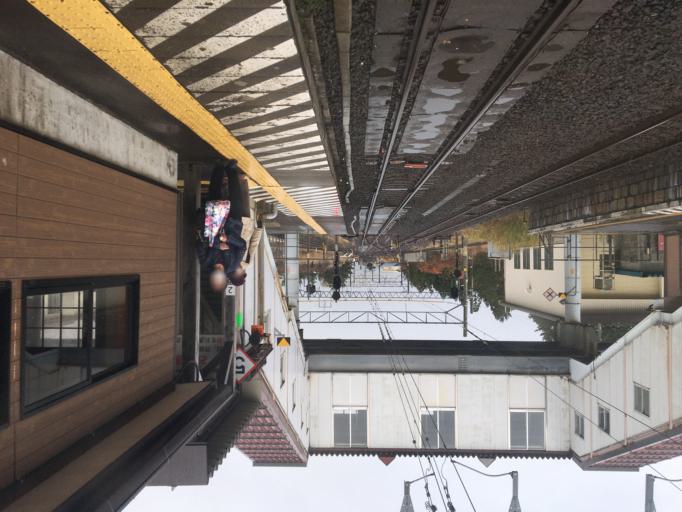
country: JP
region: Aomori
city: Aomori Shi
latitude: 41.0383
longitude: 140.6426
